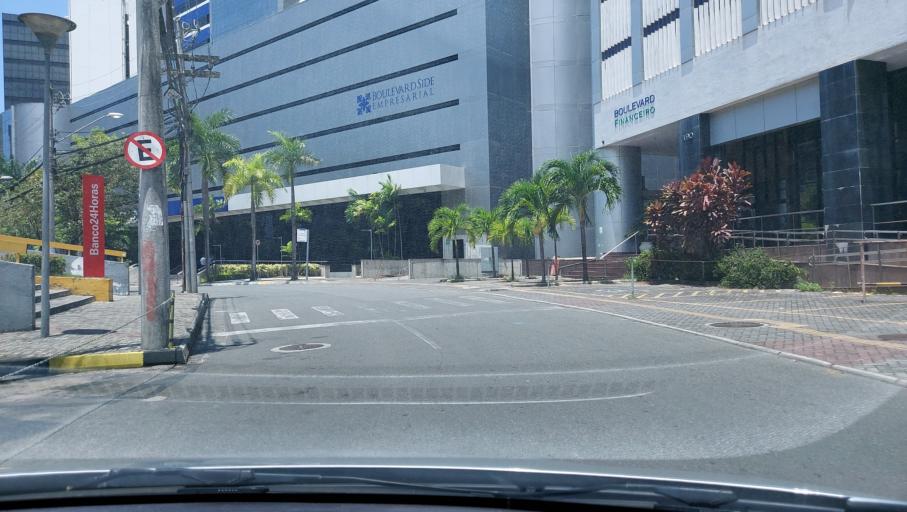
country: BR
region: Bahia
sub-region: Salvador
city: Salvador
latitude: -12.9824
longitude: -38.4555
